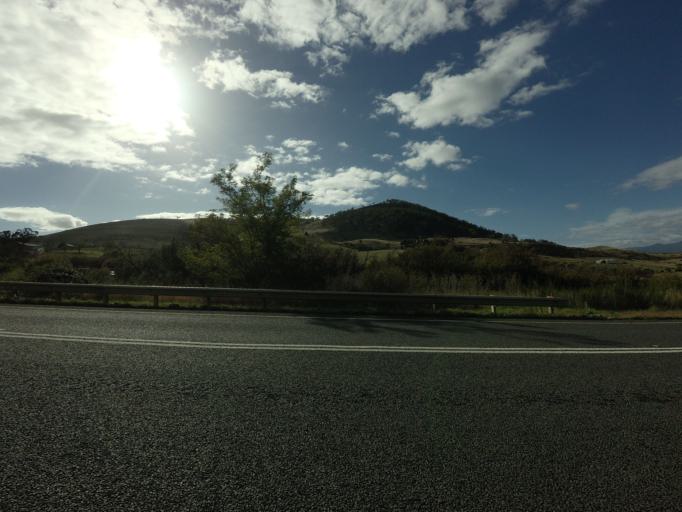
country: AU
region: Tasmania
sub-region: Derwent Valley
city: New Norfolk
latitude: -42.7197
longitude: 146.9482
